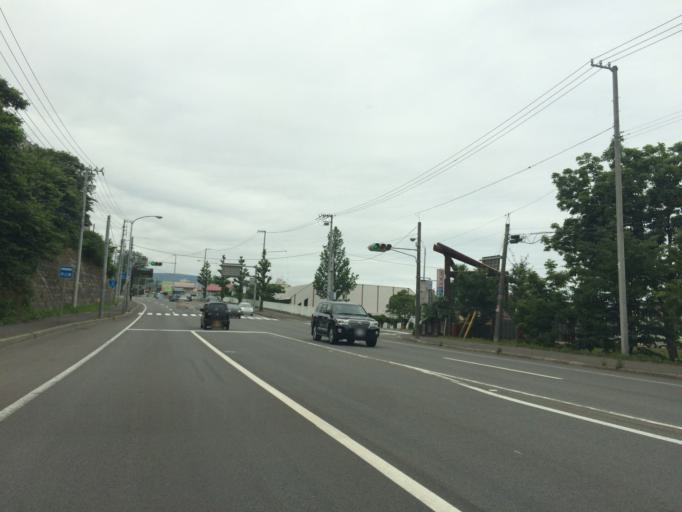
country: JP
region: Hokkaido
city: Otaru
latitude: 43.1383
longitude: 141.1673
